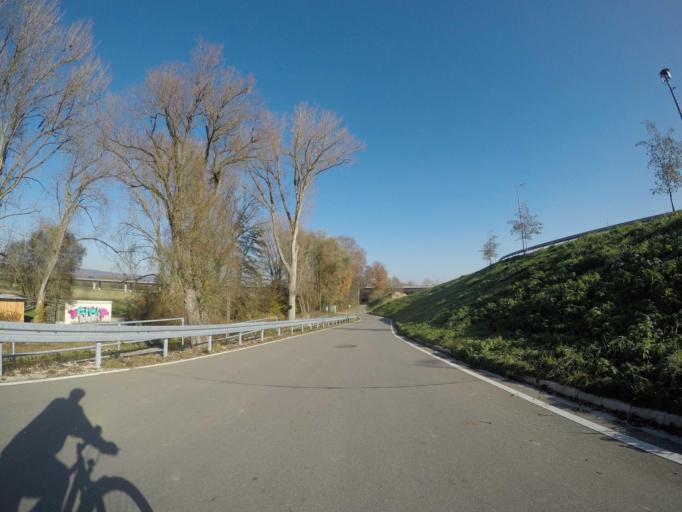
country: DE
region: Baden-Wuerttemberg
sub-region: Tuebingen Region
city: Riedlingen
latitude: 48.1532
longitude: 9.4874
